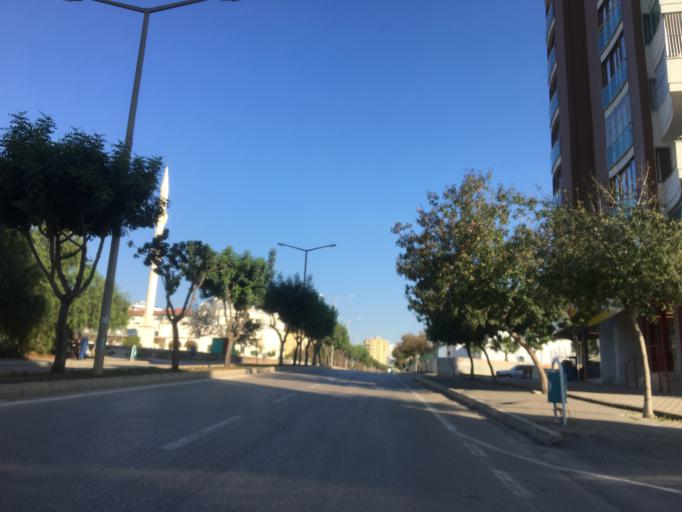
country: TR
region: Adana
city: Seyhan
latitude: 37.0285
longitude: 35.2618
